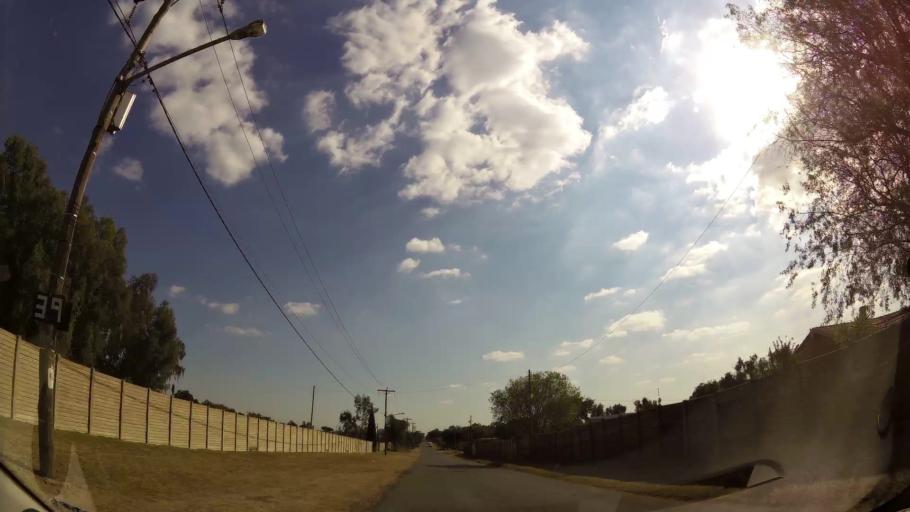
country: ZA
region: Gauteng
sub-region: Ekurhuleni Metropolitan Municipality
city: Benoni
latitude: -26.1035
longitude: 28.3539
